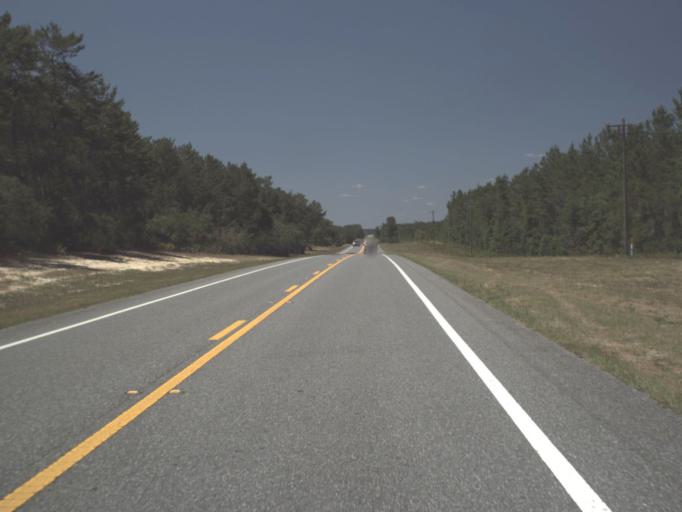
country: US
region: Florida
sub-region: Lake County
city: Astor
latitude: 29.1505
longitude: -81.6334
